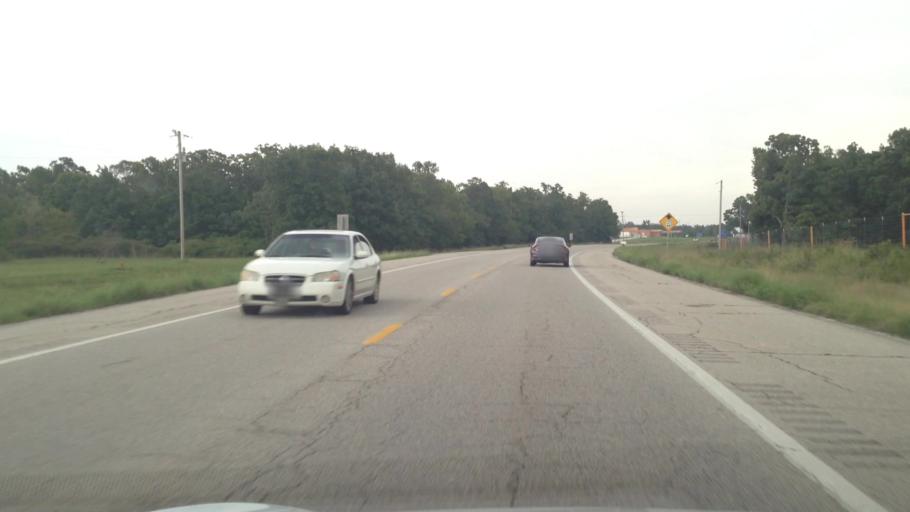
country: US
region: Kansas
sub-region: Cherokee County
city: Galena
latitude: 37.0071
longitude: -94.6206
